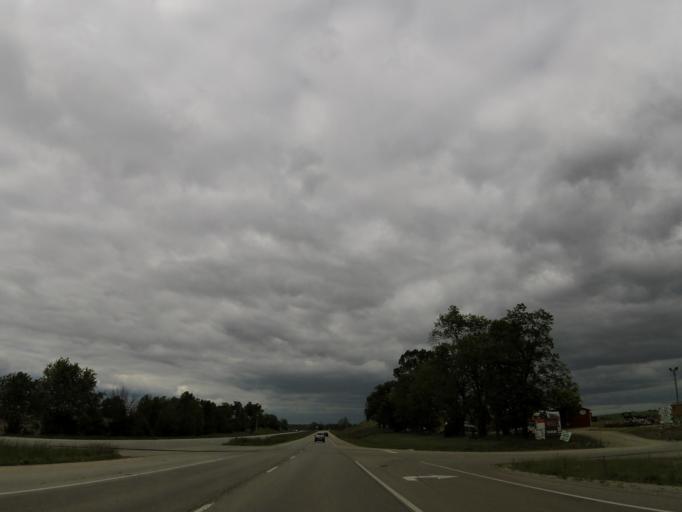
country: US
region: Kentucky
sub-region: Scott County
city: Georgetown
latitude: 38.1914
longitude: -84.5421
